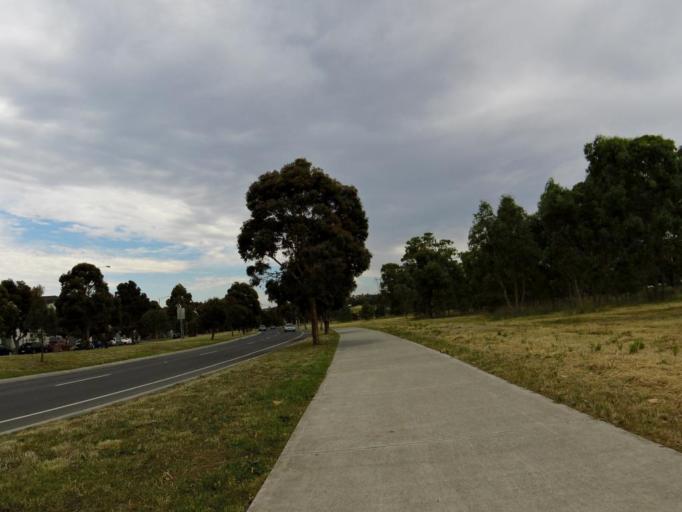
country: AU
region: Victoria
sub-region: Whittlesea
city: Mill Park
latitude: -37.6478
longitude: 145.0661
